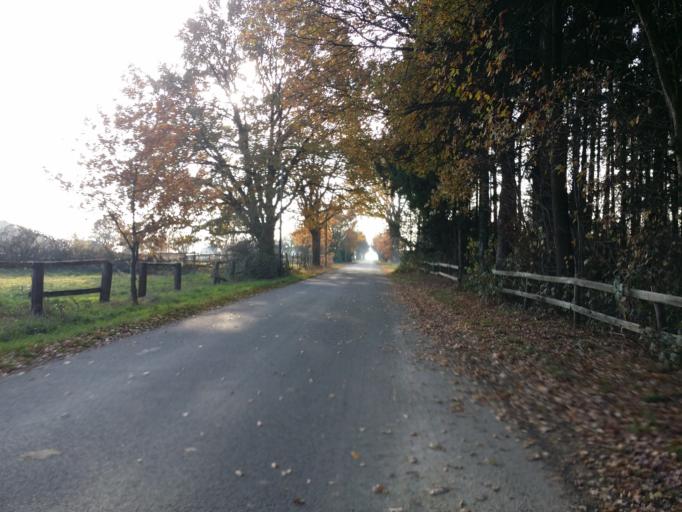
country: DE
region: Lower Saxony
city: Reessum
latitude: 53.1310
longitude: 9.1993
